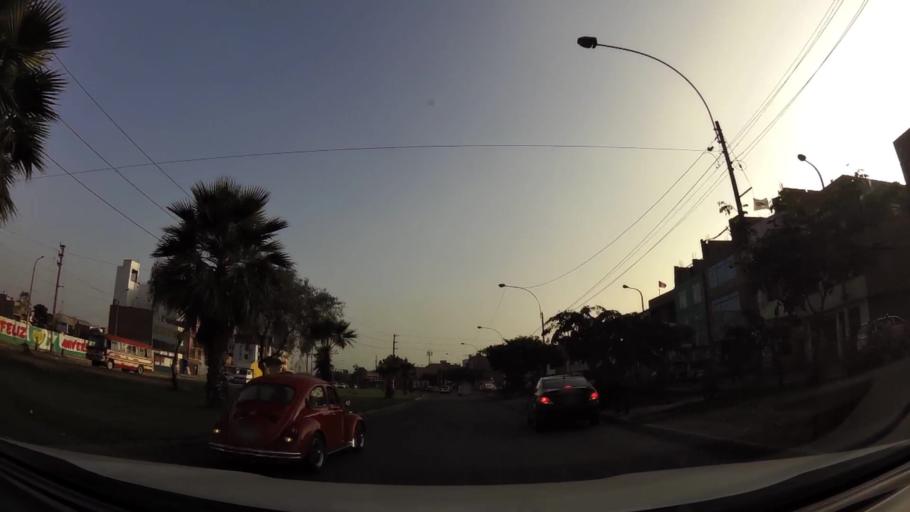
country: PE
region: Lima
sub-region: Lima
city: Independencia
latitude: -11.9646
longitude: -77.0730
